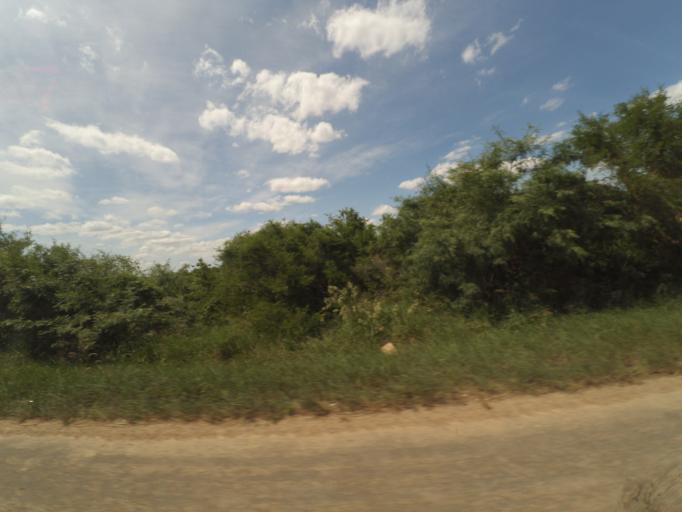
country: BO
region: Santa Cruz
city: Pailon
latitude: -17.5889
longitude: -61.9628
